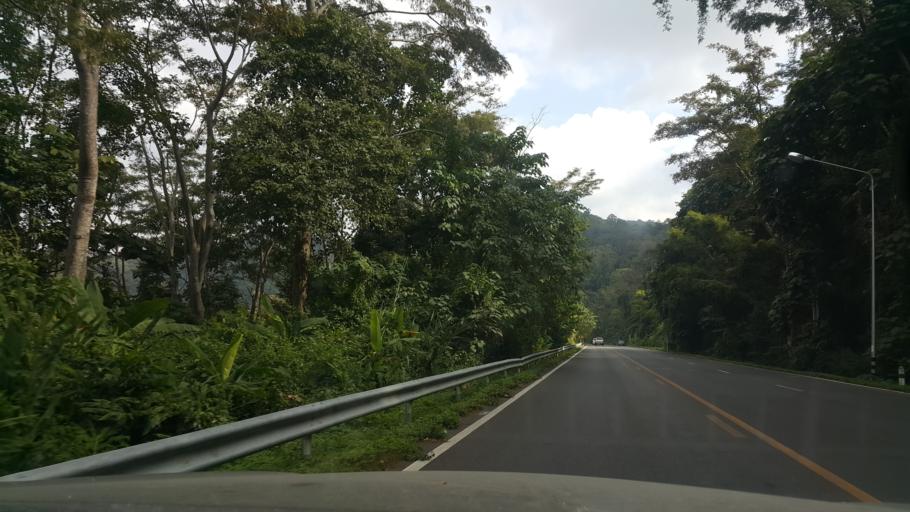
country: TH
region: Phayao
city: Phayao
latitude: 19.0596
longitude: 99.7841
